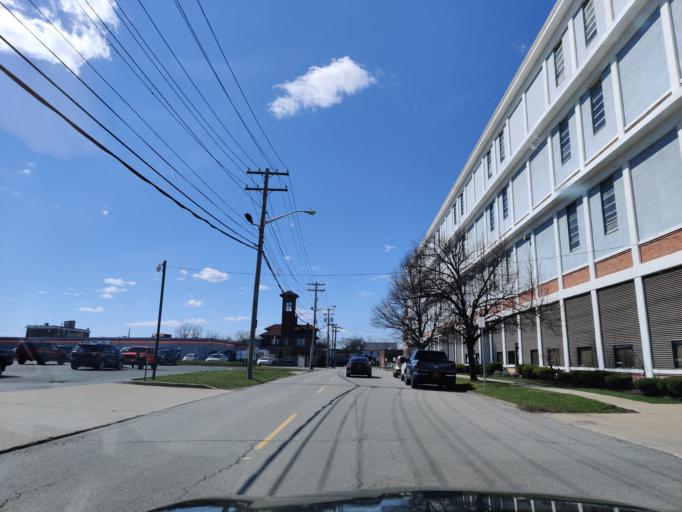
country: US
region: New York
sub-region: Erie County
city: Kenmore
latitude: 42.9420
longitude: -78.8764
